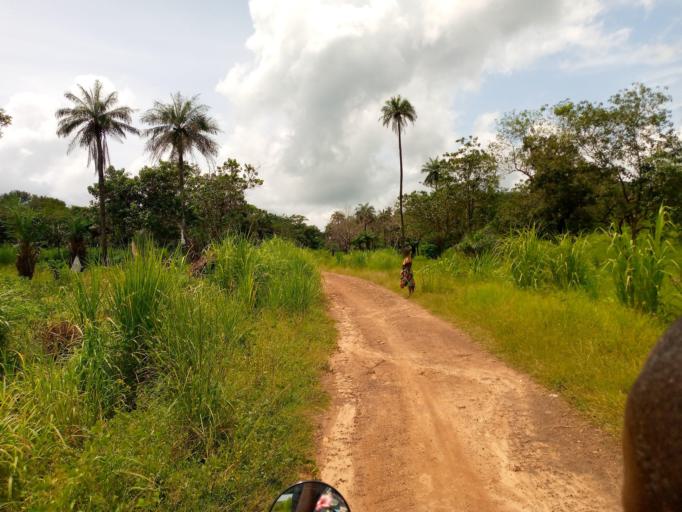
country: SL
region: Northern Province
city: Binkolo
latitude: 9.1212
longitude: -12.1335
